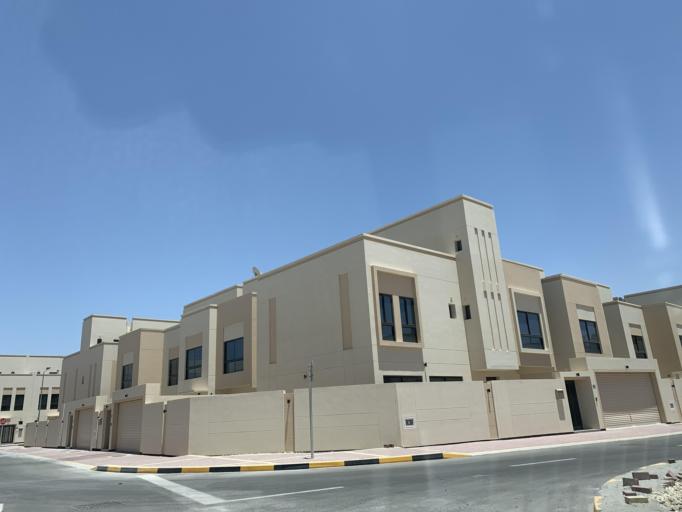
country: BH
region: Manama
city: Jidd Hafs
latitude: 26.2343
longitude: 50.4963
